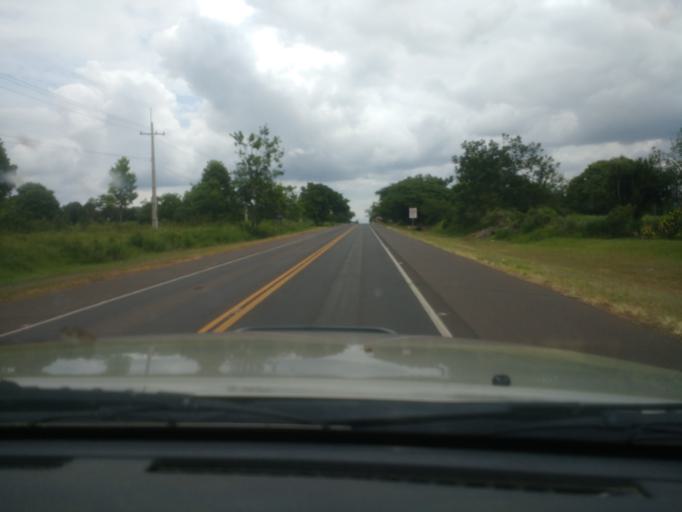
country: PY
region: Cordillera
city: Arroyos y Esteros
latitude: -25.0566
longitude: -57.1335
